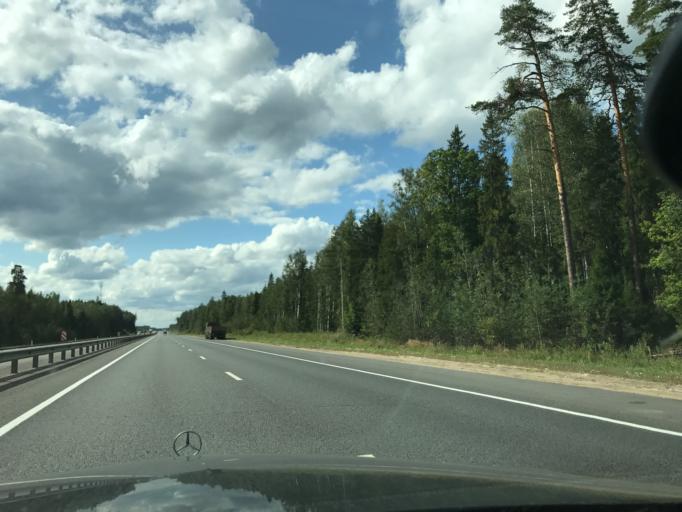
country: RU
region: Vladimir
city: Orgtrud
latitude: 56.1031
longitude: 40.7083
